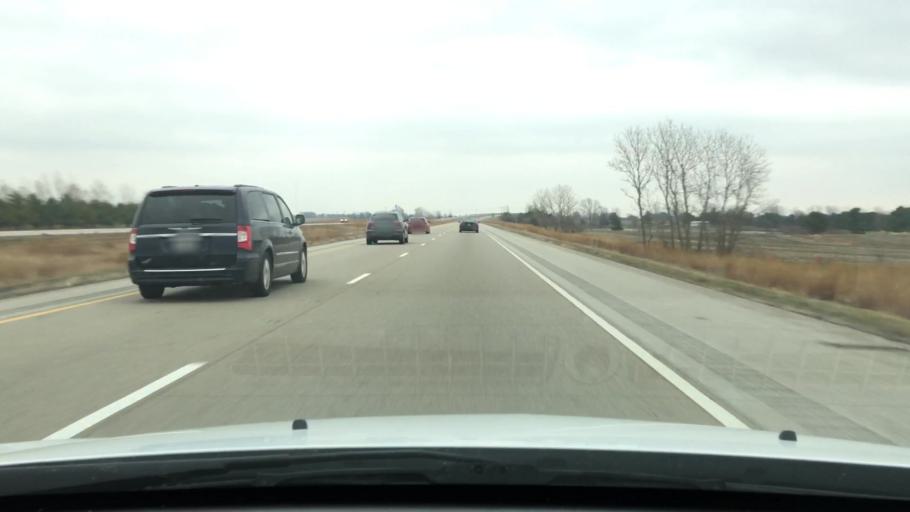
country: US
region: Illinois
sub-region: Logan County
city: Lincoln
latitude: 40.1826
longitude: -89.3385
